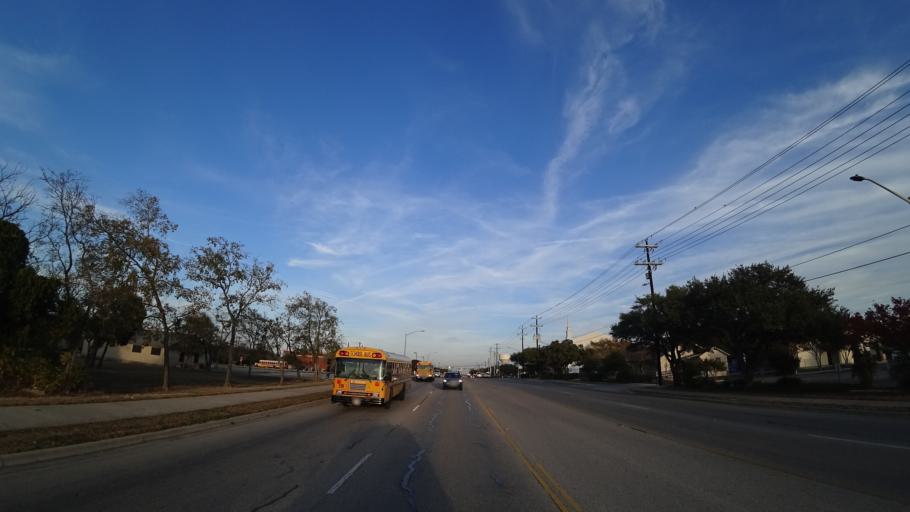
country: US
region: Texas
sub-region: Williamson County
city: Cedar Park
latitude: 30.5322
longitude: -97.8375
